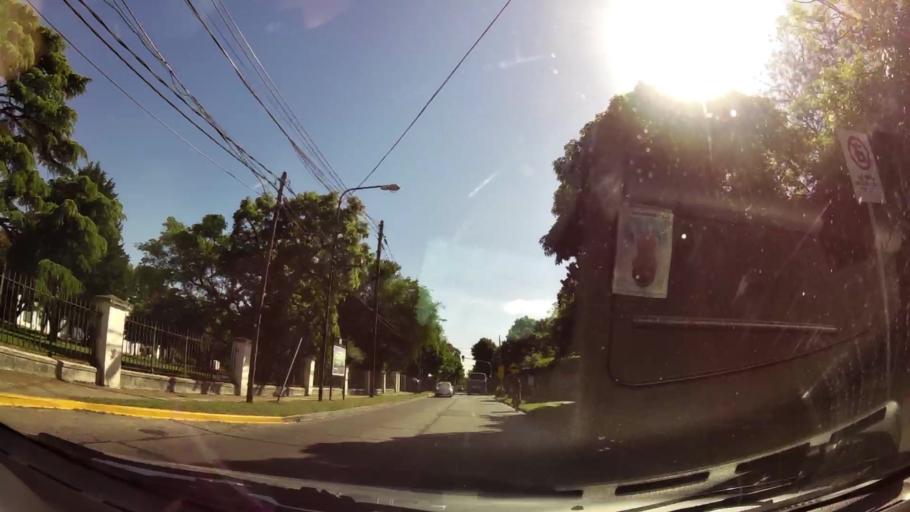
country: AR
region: Buenos Aires
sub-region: Partido de San Isidro
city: San Isidro
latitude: -34.4766
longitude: -58.5459
